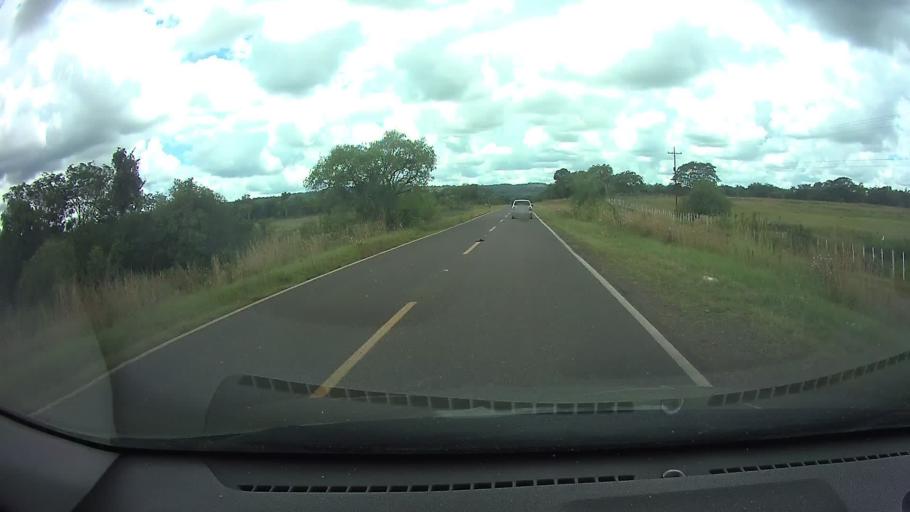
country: PY
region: Paraguari
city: Ybycui
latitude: -25.9058
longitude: -56.9793
